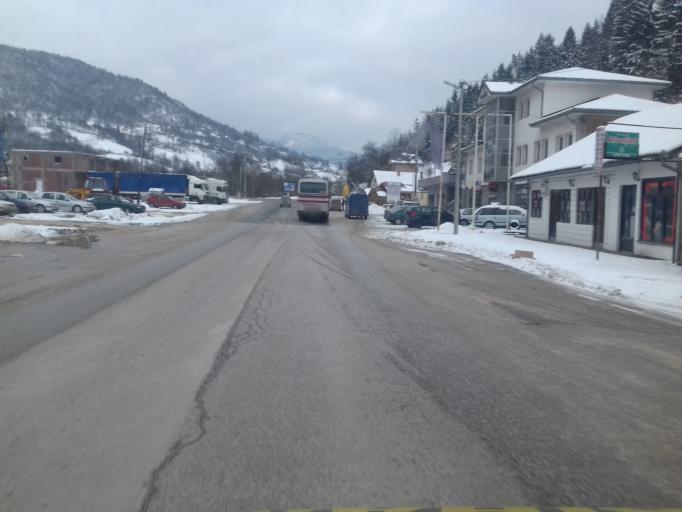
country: BA
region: Republika Srpska
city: Pale
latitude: 43.8509
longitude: 18.5388
